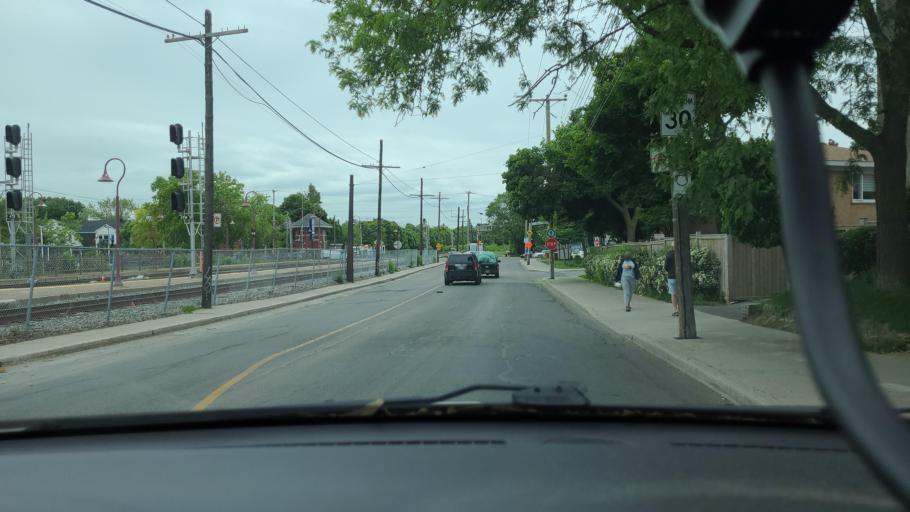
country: CA
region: Quebec
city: Montreal-Ouest
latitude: 45.4532
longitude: -73.6431
